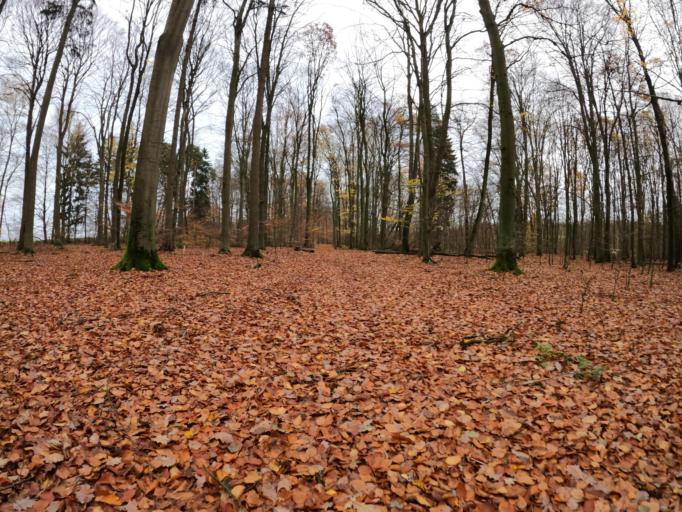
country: PL
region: West Pomeranian Voivodeship
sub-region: Powiat walecki
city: Tuczno
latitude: 53.2514
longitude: 16.2320
